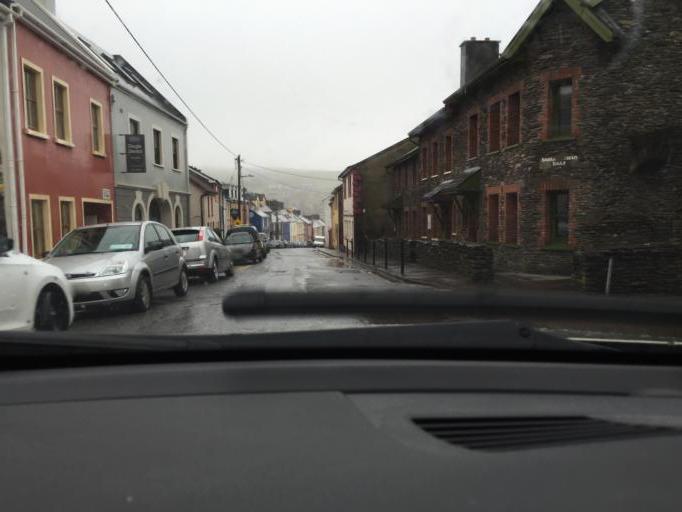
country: IE
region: Munster
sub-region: Ciarrai
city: Dingle
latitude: 52.1431
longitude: -10.2717
